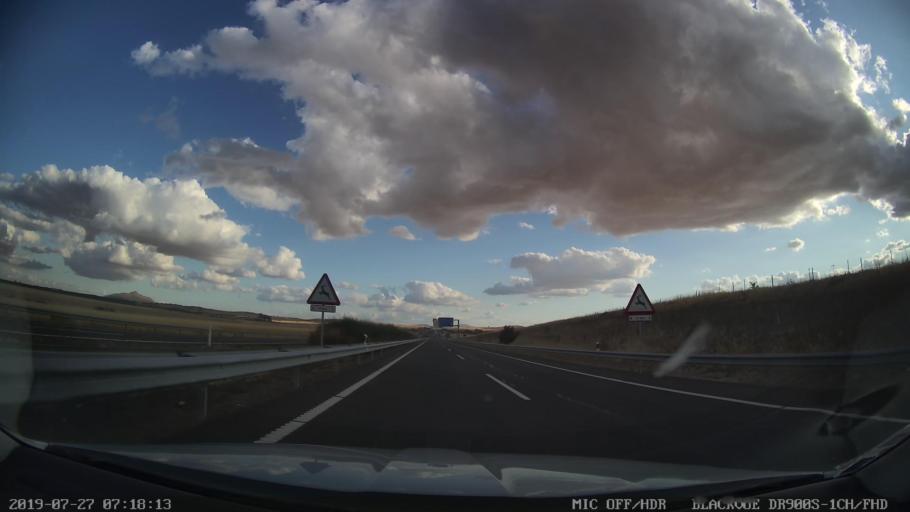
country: ES
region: Extremadura
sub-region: Provincia de Caceres
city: Trujillo
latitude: 39.4216
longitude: -5.8826
